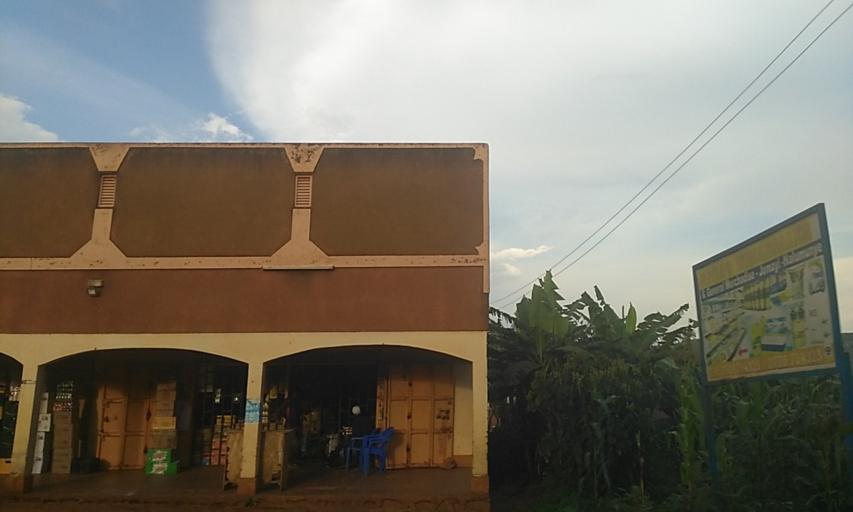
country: UG
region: Central Region
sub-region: Wakiso District
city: Kajansi
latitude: 0.2543
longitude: 32.5345
